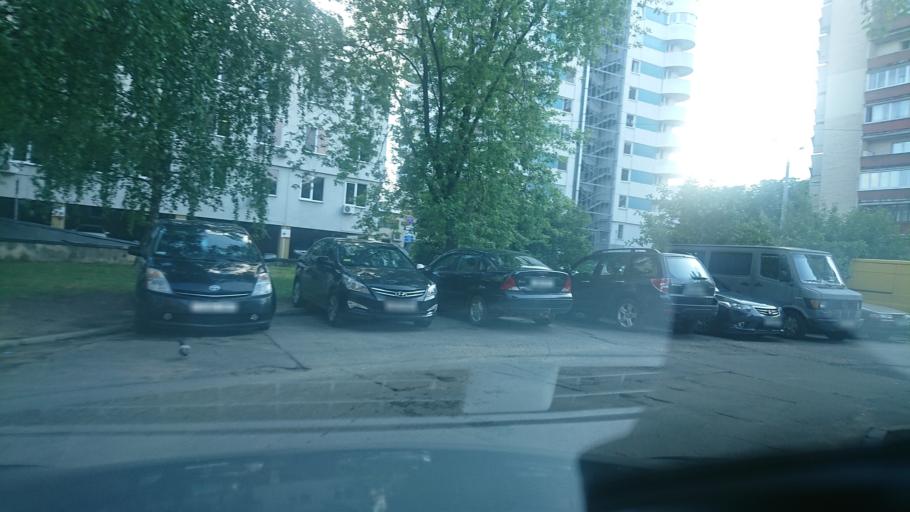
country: BY
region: Minsk
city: Minsk
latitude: 53.9224
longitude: 27.5675
